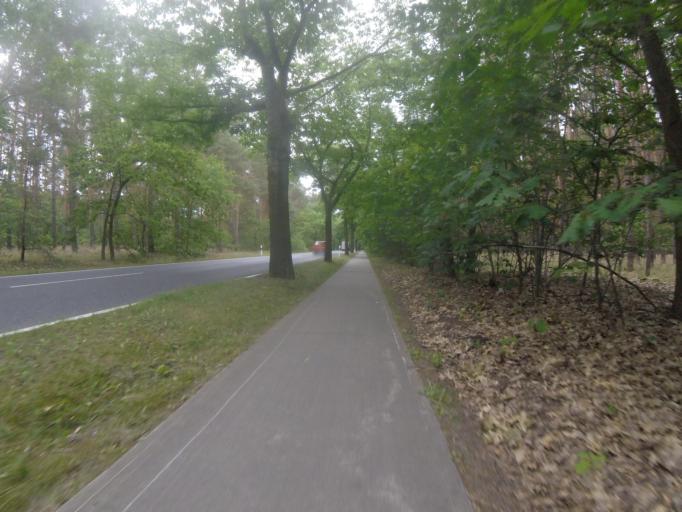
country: DE
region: Brandenburg
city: Bestensee
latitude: 52.2575
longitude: 13.6325
